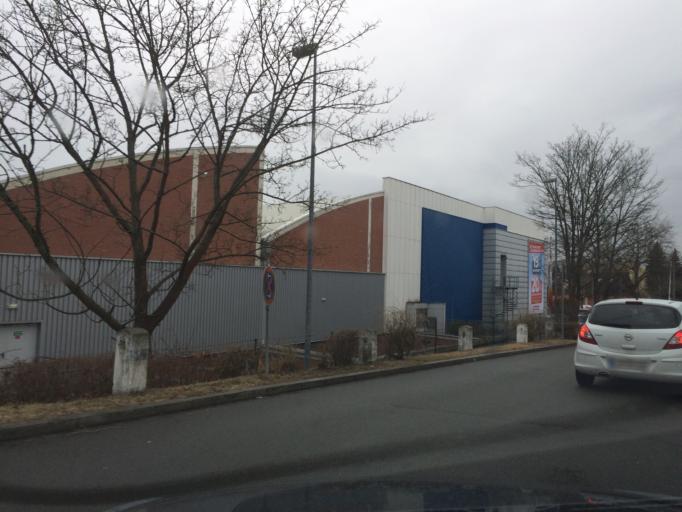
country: DE
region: Bavaria
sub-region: Regierungsbezirk Mittelfranken
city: Schwaig
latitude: 49.4618
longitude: 11.1414
